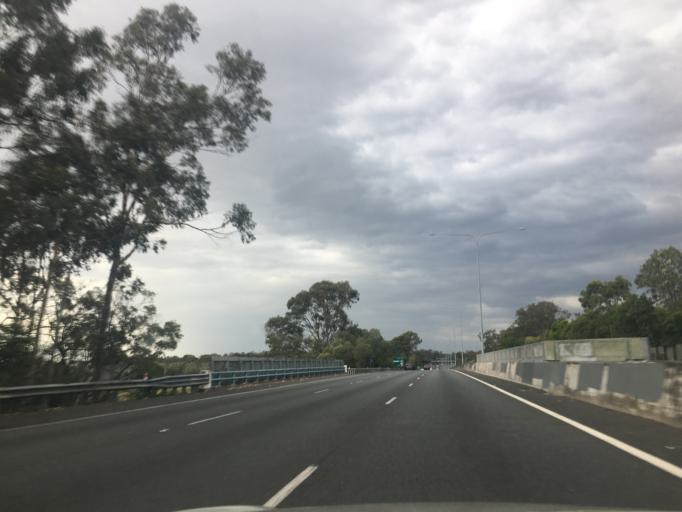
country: AU
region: Queensland
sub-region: Brisbane
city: Bald Hills
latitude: -27.3222
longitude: 153.0134
